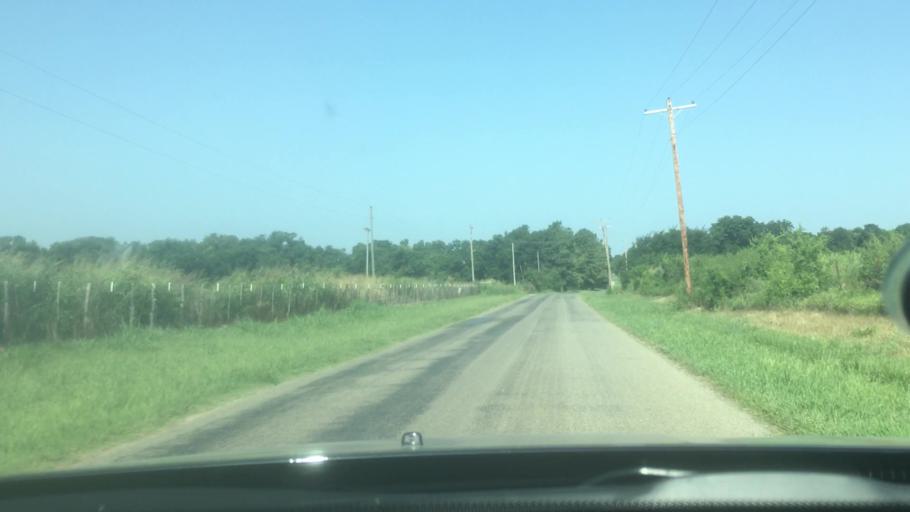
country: US
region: Oklahoma
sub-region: Bryan County
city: Calera
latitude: 33.9398
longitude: -96.4456
